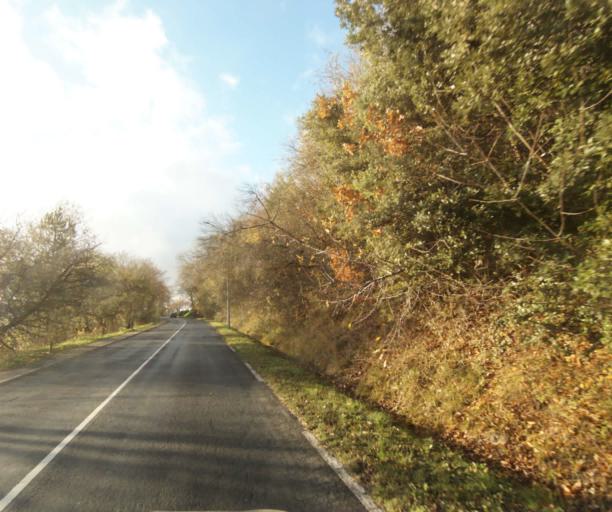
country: FR
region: Ile-de-France
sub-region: Departement des Yvelines
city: Meulan-en-Yvelines
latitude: 49.0091
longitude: 1.9202
